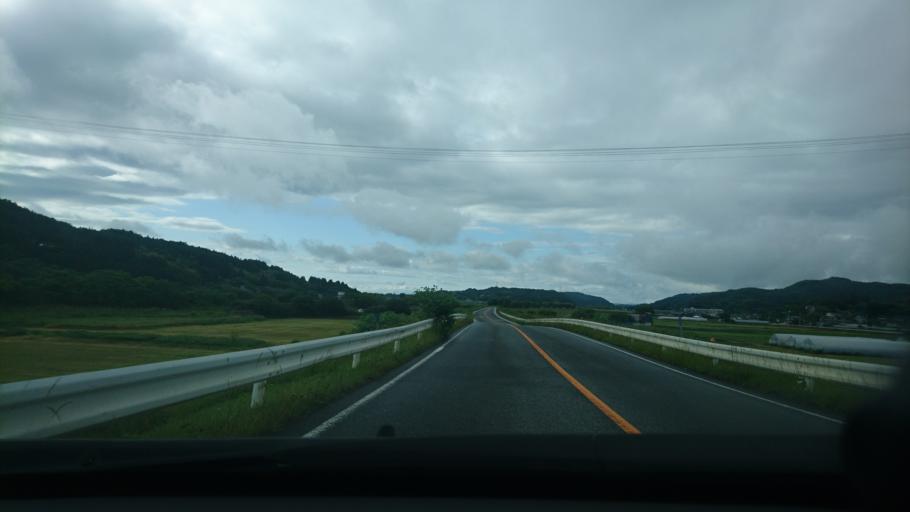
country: JP
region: Miyagi
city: Wakuya
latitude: 38.6400
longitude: 141.2881
